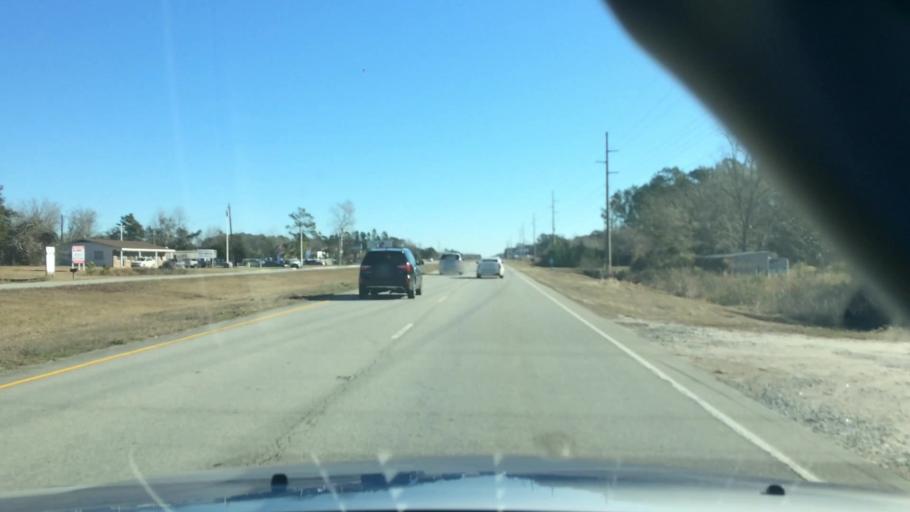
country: US
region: North Carolina
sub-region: Brunswick County
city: Sunset Beach
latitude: 33.9486
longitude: -78.4868
